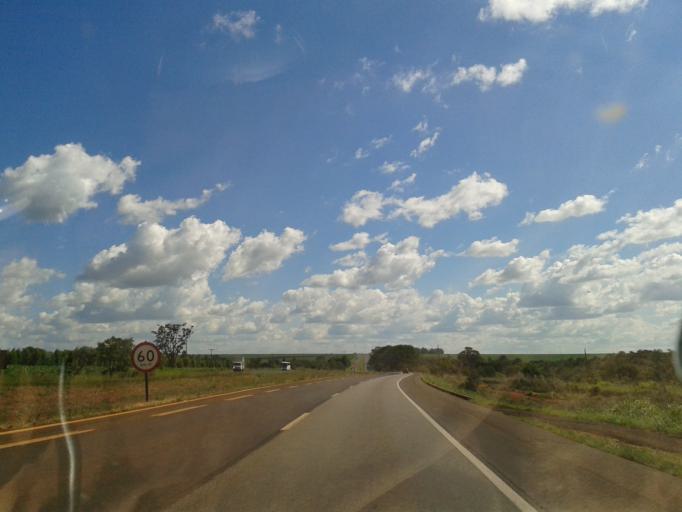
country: BR
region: Goias
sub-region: Morrinhos
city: Morrinhos
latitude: -17.8126
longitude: -49.2098
